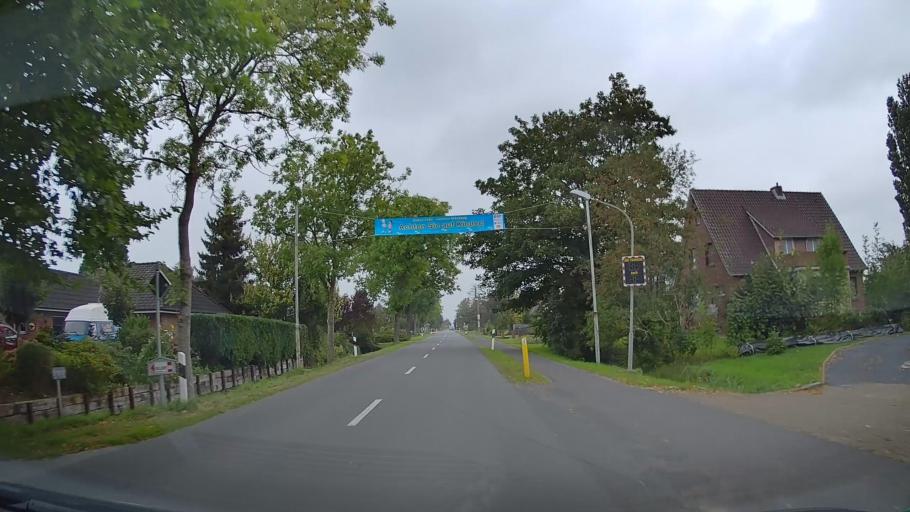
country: DE
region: Lower Saxony
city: Balje
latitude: 53.8264
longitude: 9.1328
